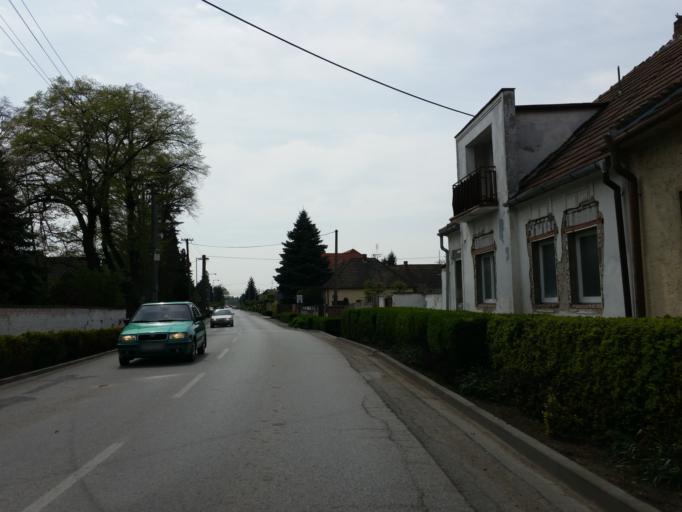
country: SK
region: Trnavsky
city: Leopoldov
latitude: 48.4457
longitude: 17.7679
